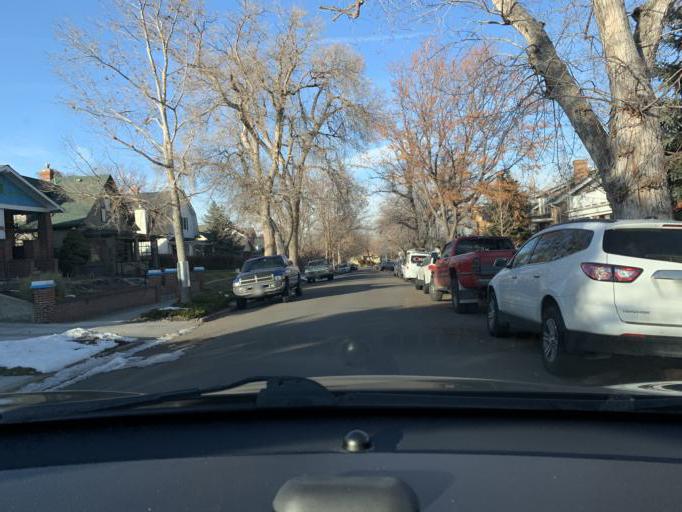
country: US
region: Colorado
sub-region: Adams County
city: Berkley
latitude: 39.7752
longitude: -105.0334
